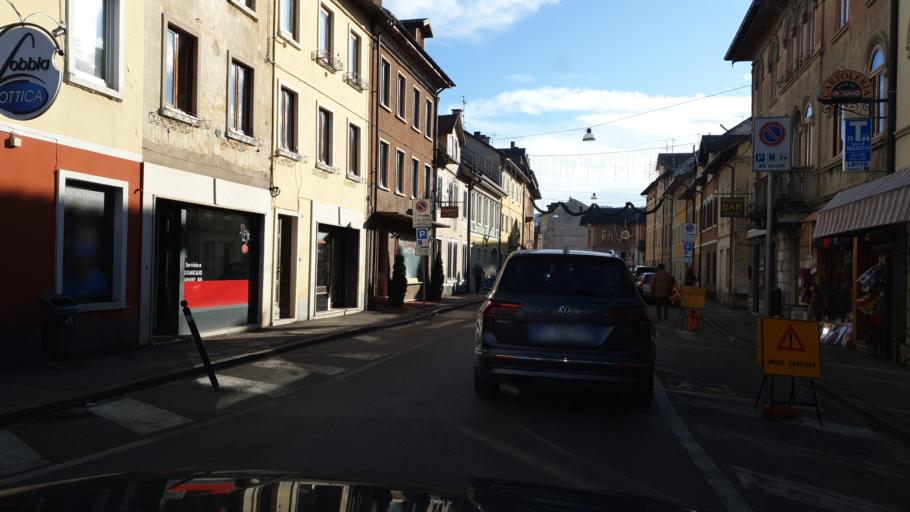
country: IT
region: Veneto
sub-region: Provincia di Vicenza
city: Asiago
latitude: 45.8720
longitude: 11.5101
